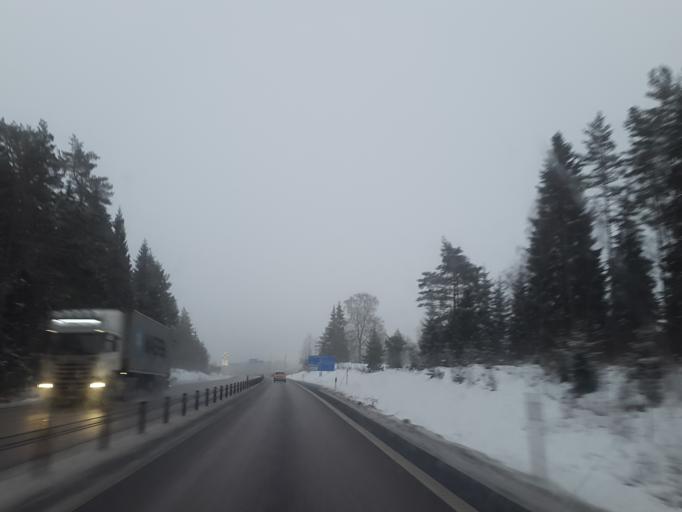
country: SE
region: Vaestra Goetaland
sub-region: Ulricehamns Kommun
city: Ulricehamn
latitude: 57.7809
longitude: 13.6557
